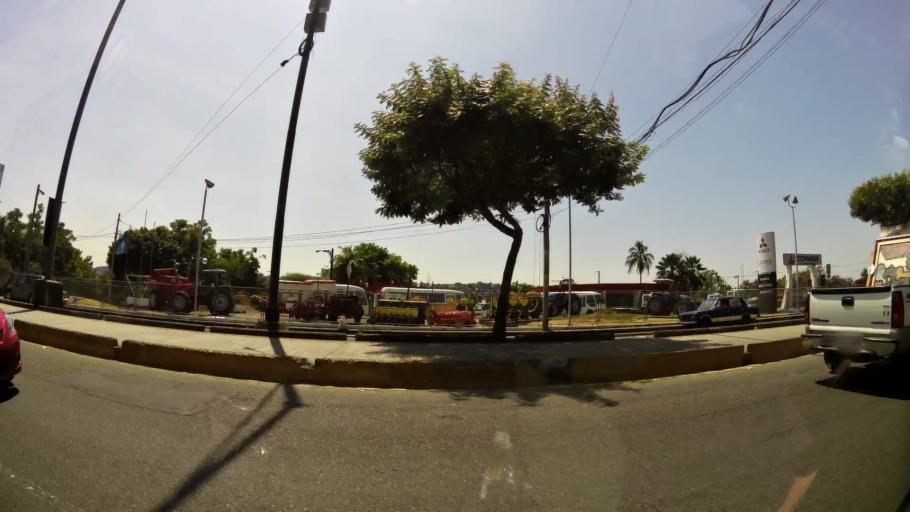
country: EC
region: Guayas
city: Guayaquil
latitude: -2.1638
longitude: -79.9248
